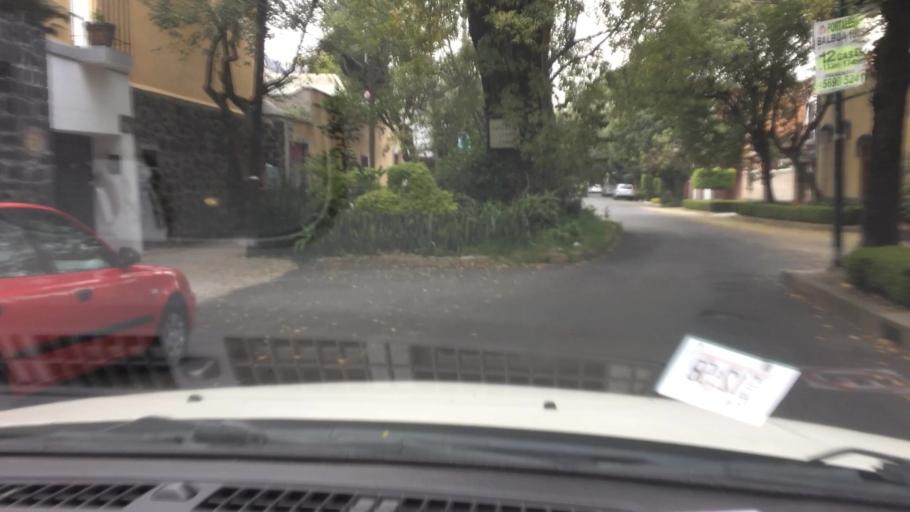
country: MX
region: Mexico City
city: Coyoacan
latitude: 19.3514
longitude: -99.1666
